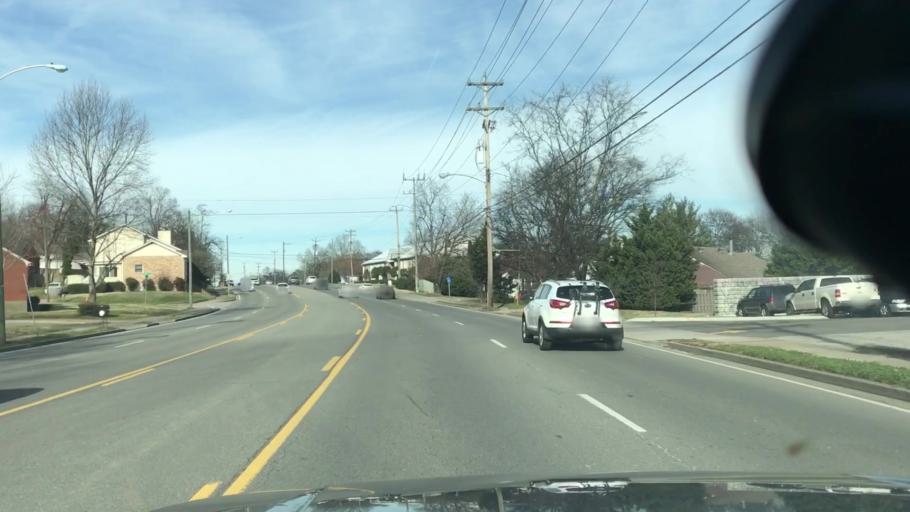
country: US
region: Tennessee
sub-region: Davidson County
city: Belle Meade
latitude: 36.1387
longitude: -86.8575
